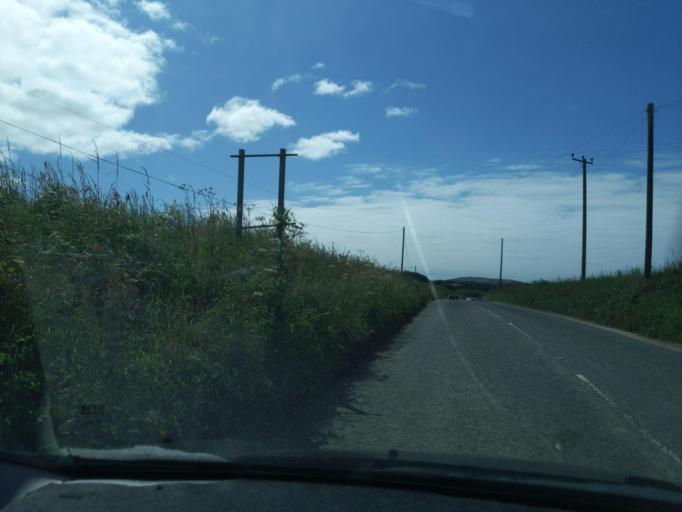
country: GB
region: England
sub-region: Cornwall
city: Perranporth
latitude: 50.2984
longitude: -5.1441
